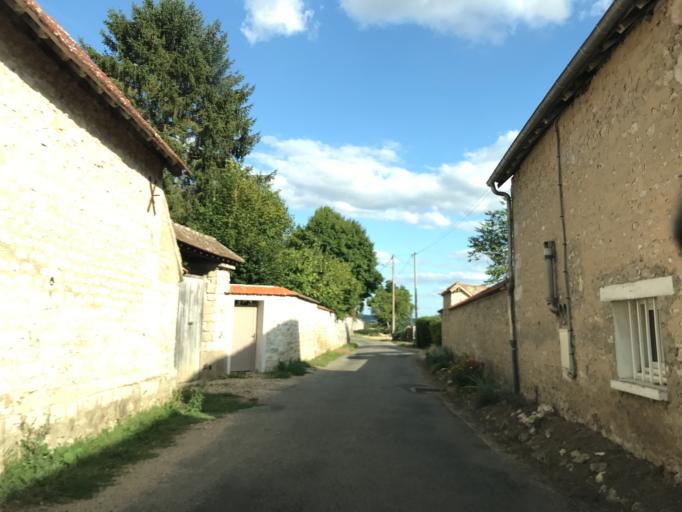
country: FR
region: Haute-Normandie
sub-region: Departement de l'Eure
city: Courcelles-sur-Seine
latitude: 49.1689
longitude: 1.4013
